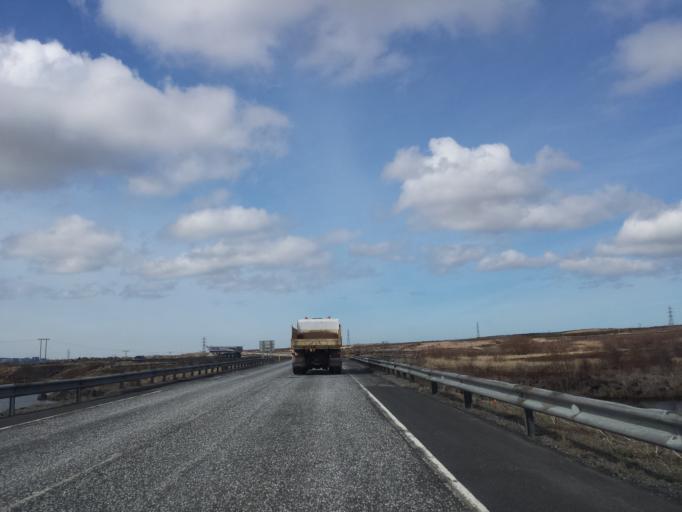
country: IS
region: Capital Region
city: Mosfellsbaer
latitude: 64.0887
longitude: -21.6961
